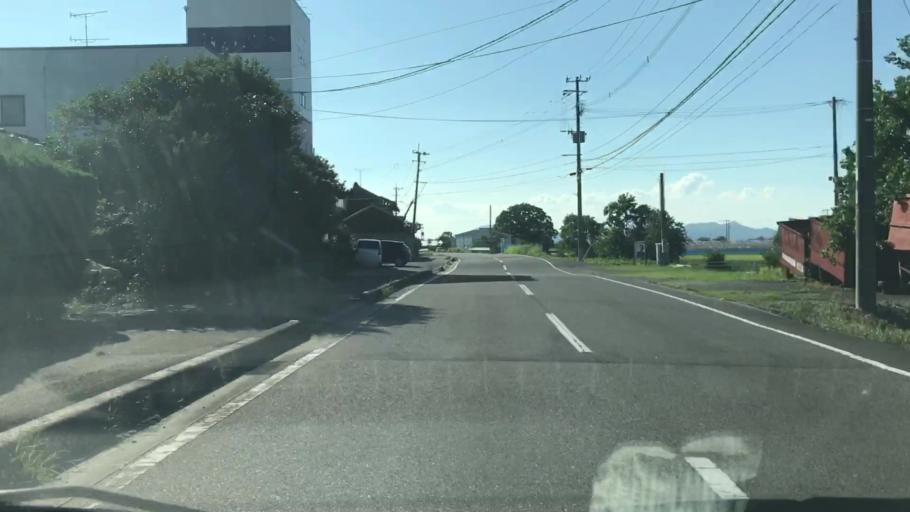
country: JP
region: Saga Prefecture
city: Saga-shi
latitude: 33.1906
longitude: 130.2854
